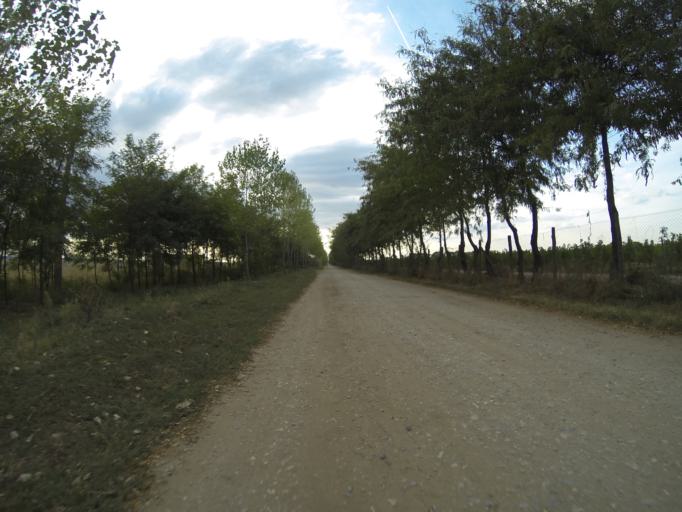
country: RO
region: Dolj
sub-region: Comuna Segarcea
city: Segarcea
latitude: 44.1020
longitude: 23.7172
